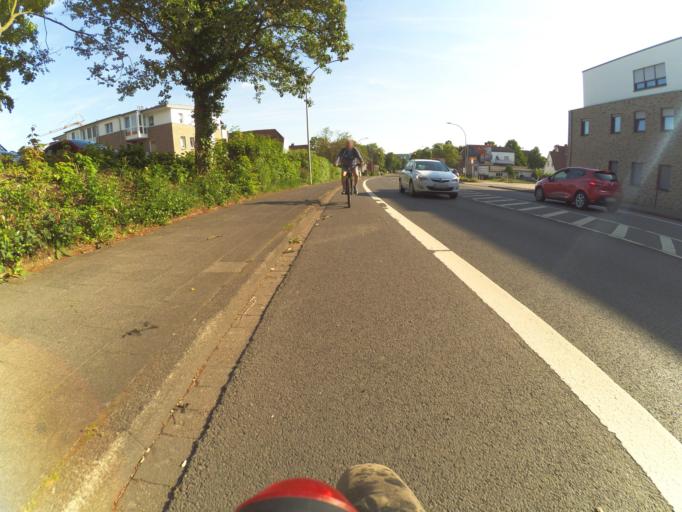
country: DE
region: North Rhine-Westphalia
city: Ibbenburen
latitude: 52.2756
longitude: 7.7113
